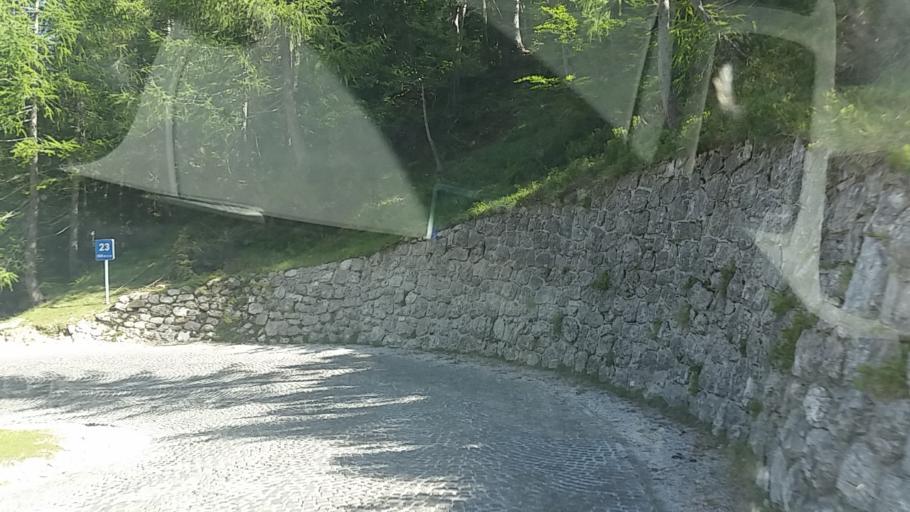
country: SI
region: Kranjska Gora
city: Kranjska Gora
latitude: 46.4378
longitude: 13.7476
